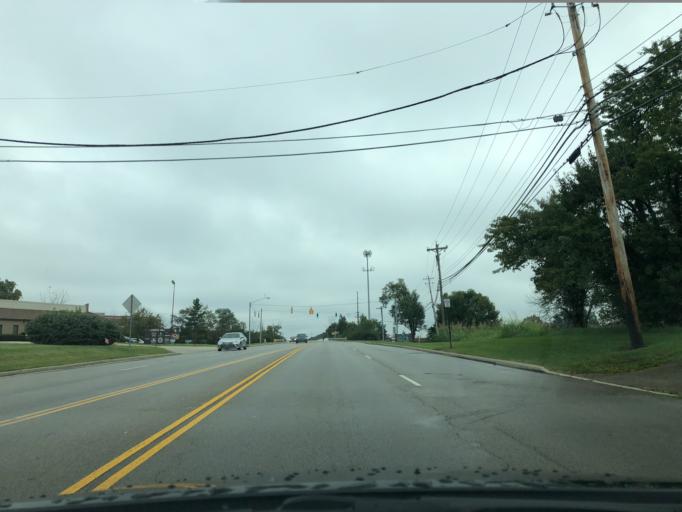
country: US
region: Ohio
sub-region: Hamilton County
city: Highpoint
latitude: 39.2828
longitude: -84.3698
